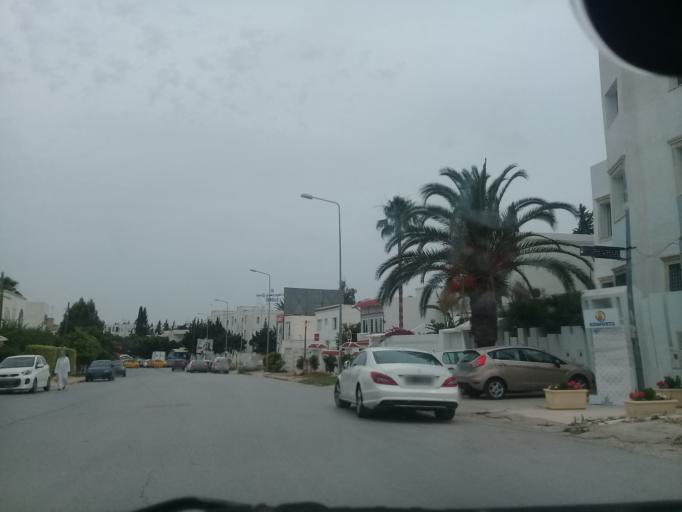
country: TN
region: Tunis
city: Tunis
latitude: 36.8410
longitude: 10.1604
